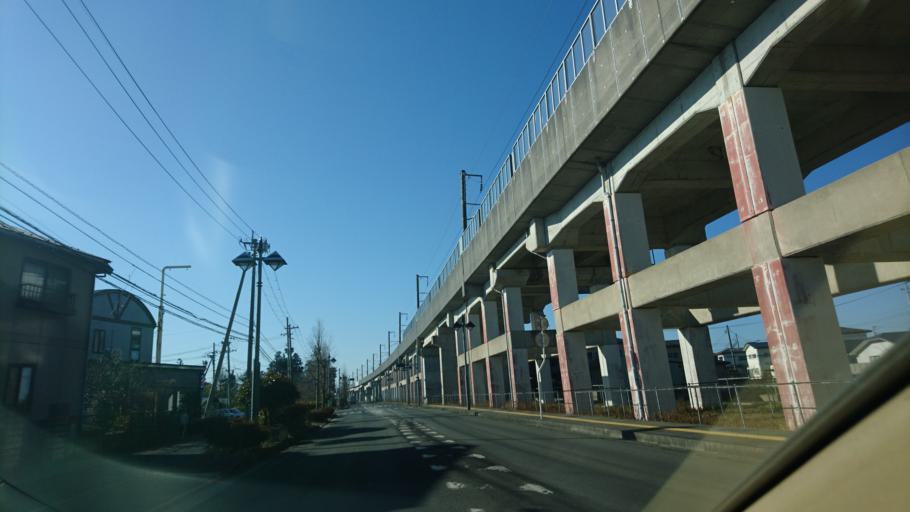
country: JP
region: Miyagi
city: Furukawa
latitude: 38.5840
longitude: 140.9719
